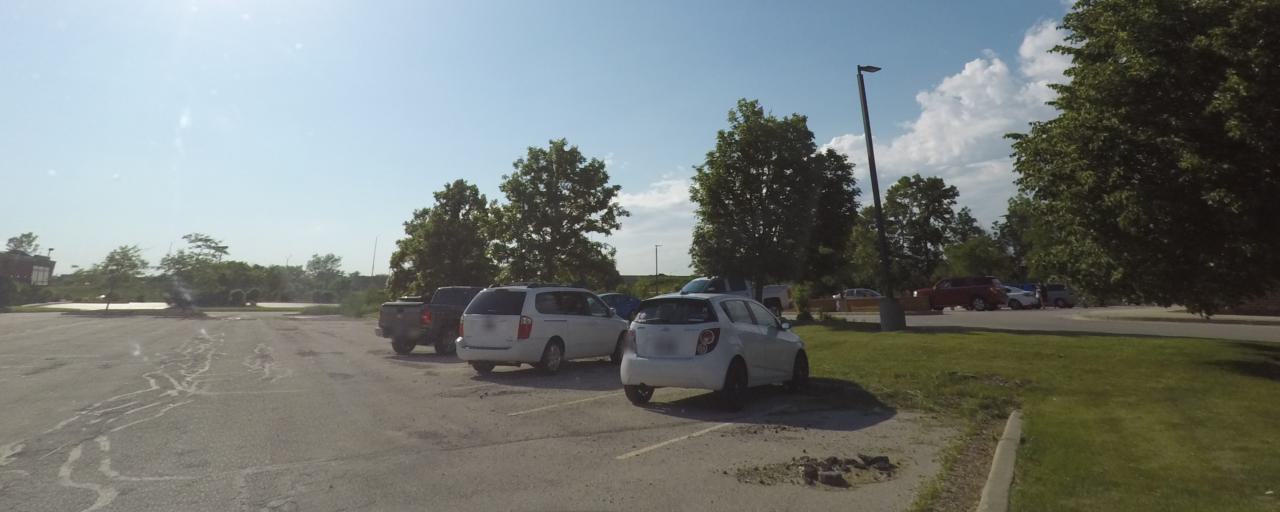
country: US
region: Wisconsin
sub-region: Waukesha County
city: New Berlin
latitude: 42.9509
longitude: -88.1064
